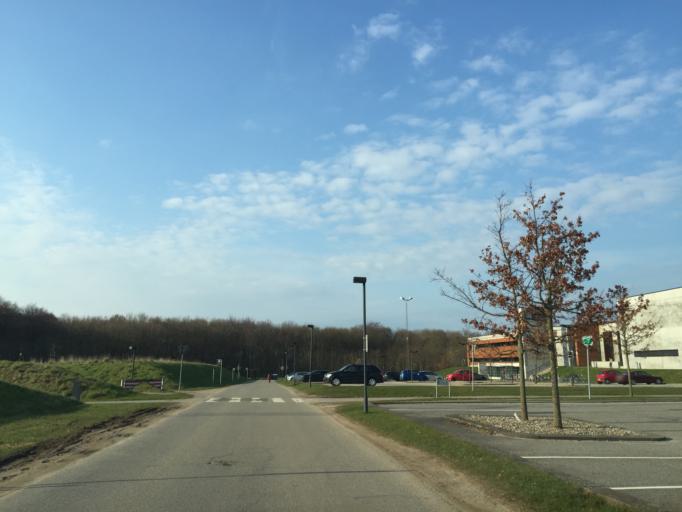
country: DK
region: South Denmark
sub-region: Odense Kommune
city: Neder Holluf
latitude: 55.3696
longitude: 10.4247
